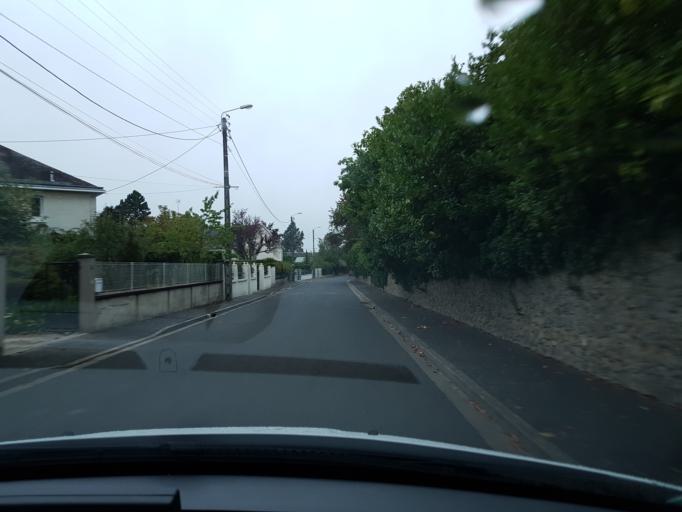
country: FR
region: Centre
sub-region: Departement d'Indre-et-Loire
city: Saint-Avertin
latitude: 47.3653
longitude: 0.7473
